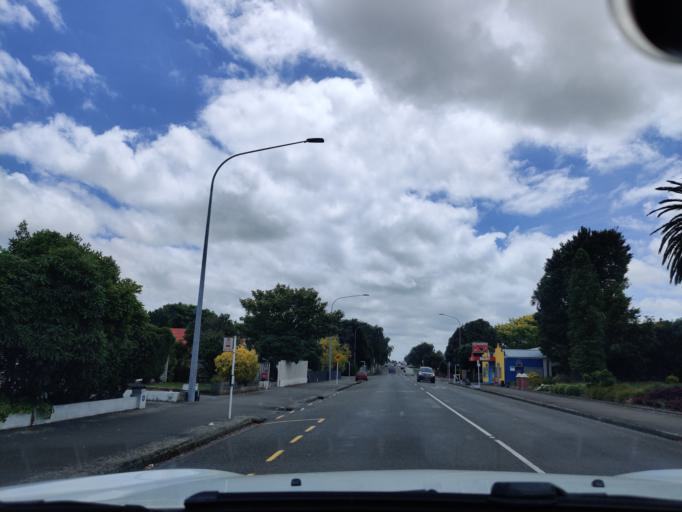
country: NZ
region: Manawatu-Wanganui
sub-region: Palmerston North City
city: Palmerston North
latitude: -40.3572
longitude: 175.6294
